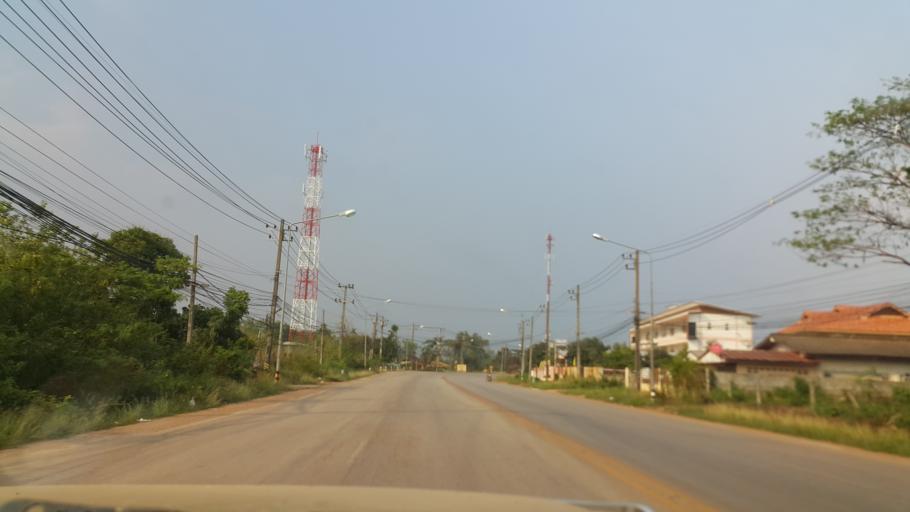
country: TH
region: Nakhon Phanom
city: That Phanom
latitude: 16.9532
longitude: 104.7222
